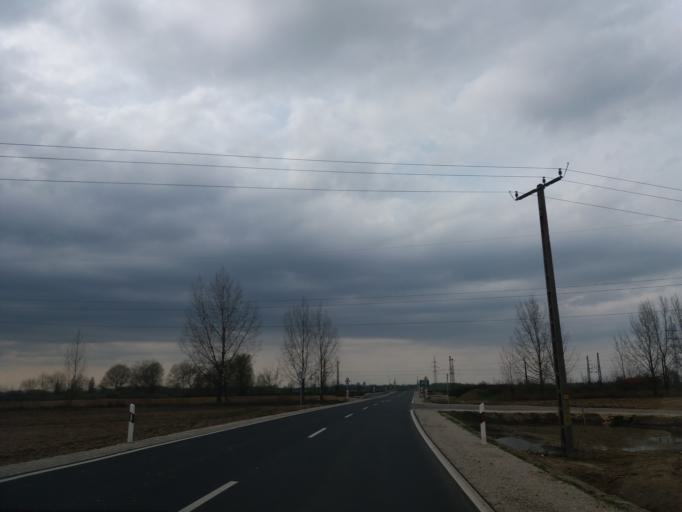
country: HU
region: Szabolcs-Szatmar-Bereg
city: Kisvarda
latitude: 48.2007
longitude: 22.0727
